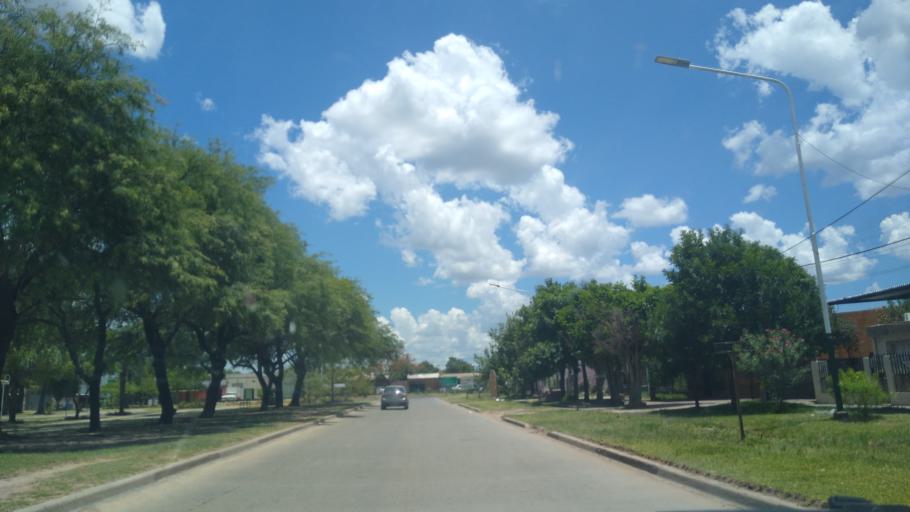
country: AR
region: Chaco
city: Presidencia Roque Saenz Pena
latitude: -26.7740
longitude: -60.4441
